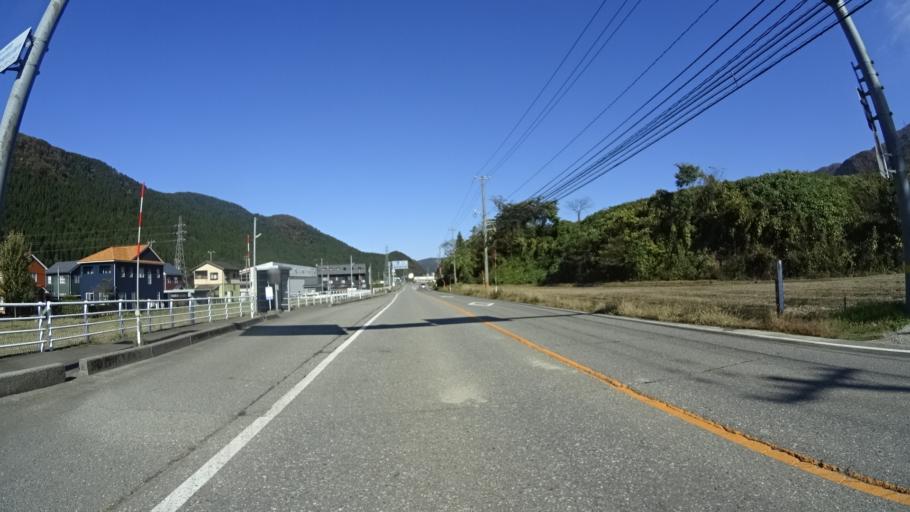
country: JP
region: Ishikawa
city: Tsurugi-asahimachi
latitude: 36.4203
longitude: 136.6313
